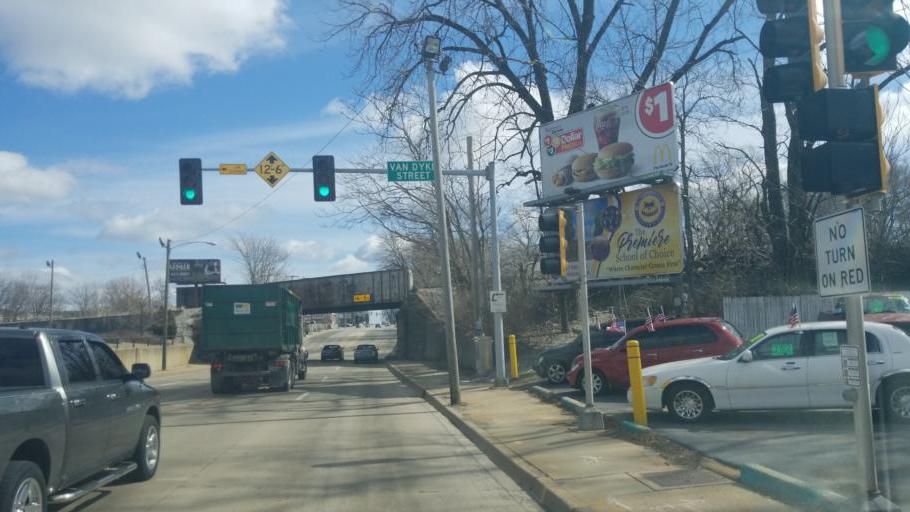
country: US
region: Illinois
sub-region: Macon County
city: Decatur
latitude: 39.8455
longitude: -88.9684
